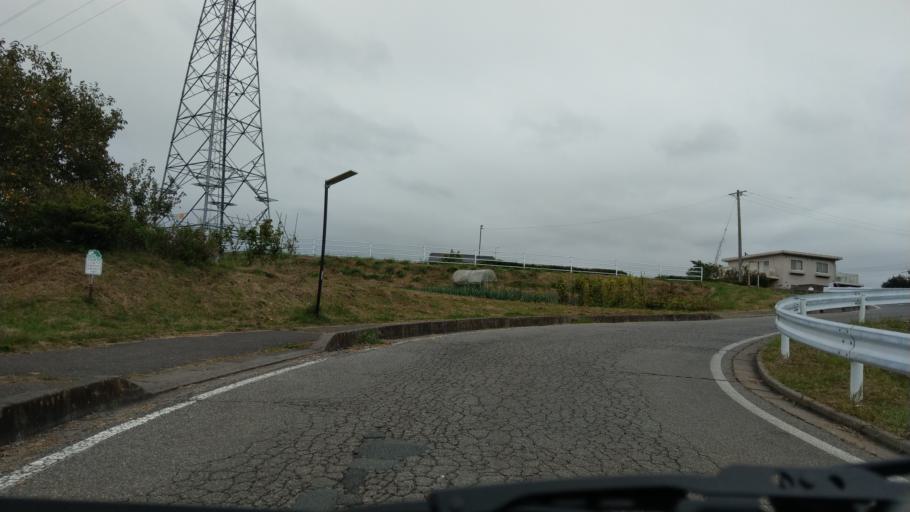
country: JP
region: Nagano
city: Komoro
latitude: 36.3118
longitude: 138.4333
